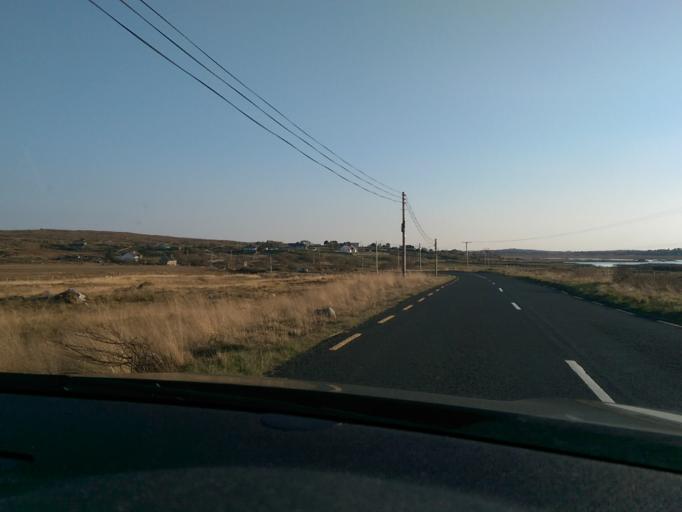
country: IE
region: Connaught
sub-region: County Galway
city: Oughterard
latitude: 53.3265
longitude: -9.5462
